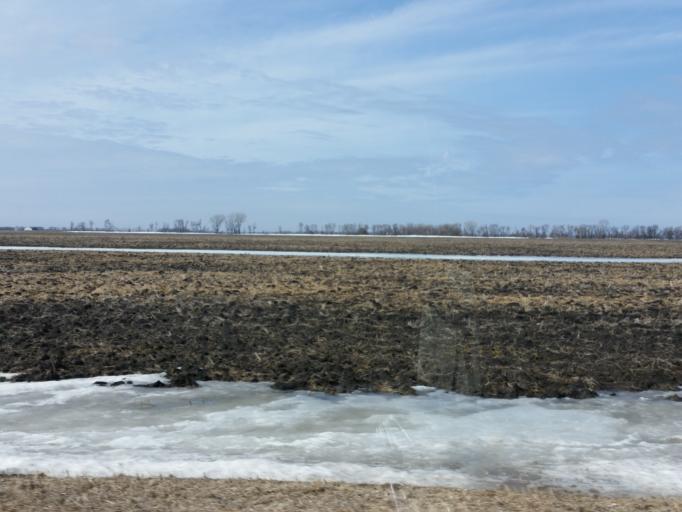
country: US
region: North Dakota
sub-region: Walsh County
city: Grafton
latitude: 48.3426
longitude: -97.2111
